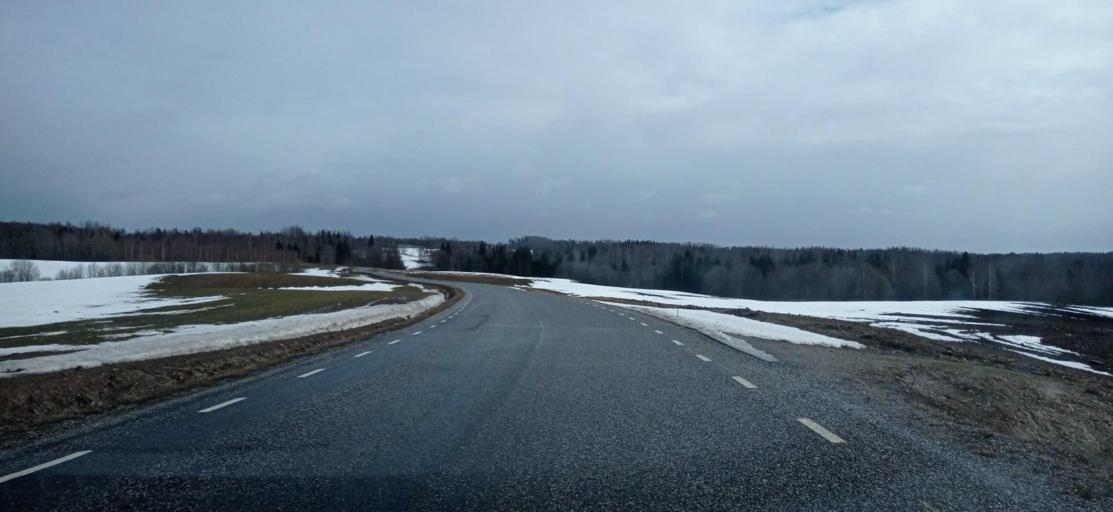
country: EE
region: Tartu
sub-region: Noo vald
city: Noo
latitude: 58.0828
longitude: 26.6666
